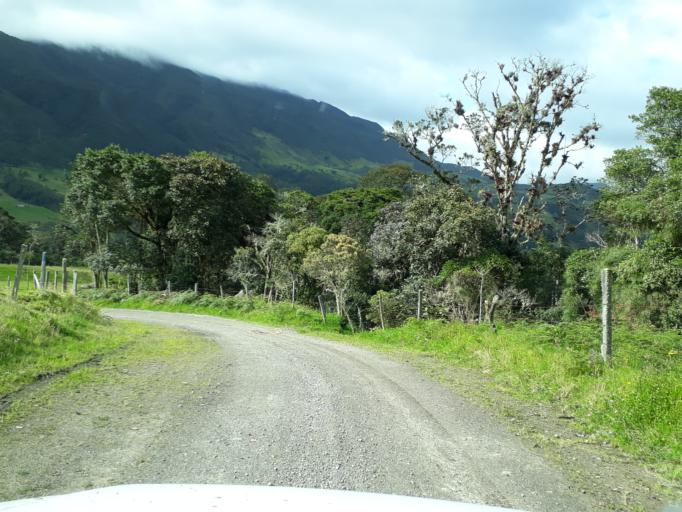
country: CO
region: Cundinamarca
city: Junin
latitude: 4.8148
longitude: -73.7732
